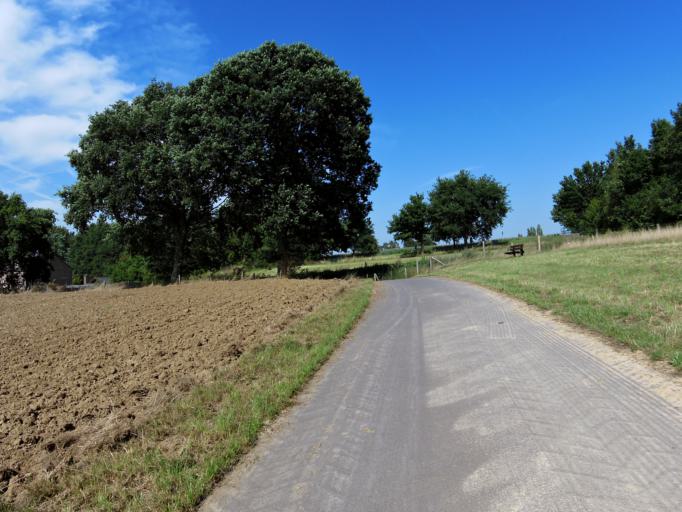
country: NL
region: Limburg
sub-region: Gemeente Voerendaal
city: Voerendaal
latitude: 50.8978
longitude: 5.9312
